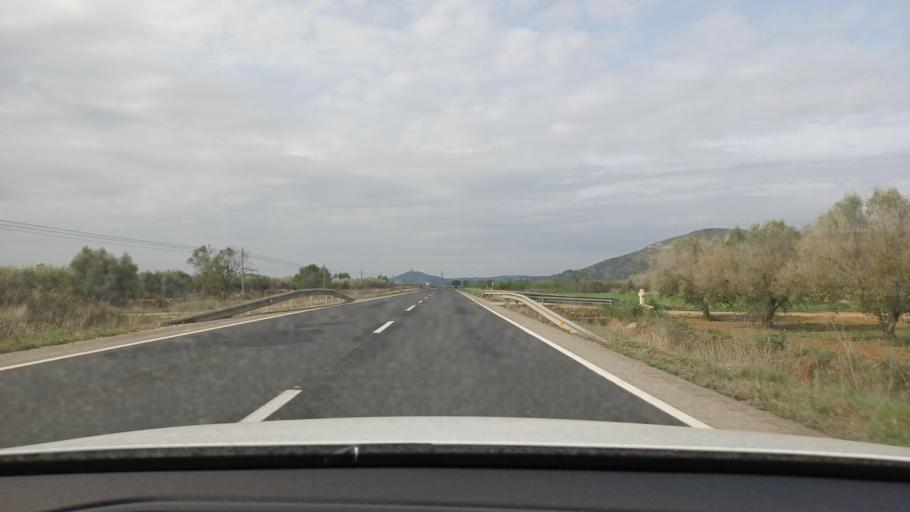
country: ES
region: Catalonia
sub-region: Provincia de Tarragona
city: Ulldecona
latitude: 40.6248
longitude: 0.4782
